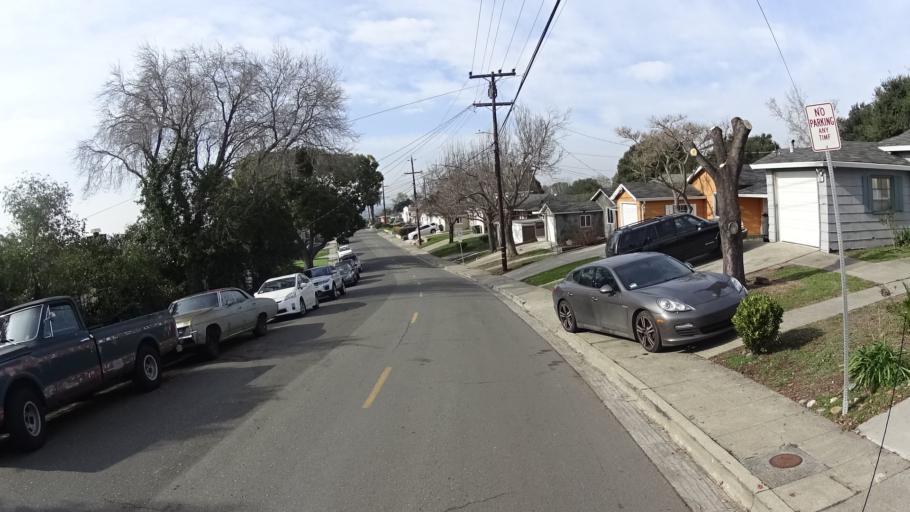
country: US
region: California
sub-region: Alameda County
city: Hayward
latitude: 37.6661
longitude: -122.0691
